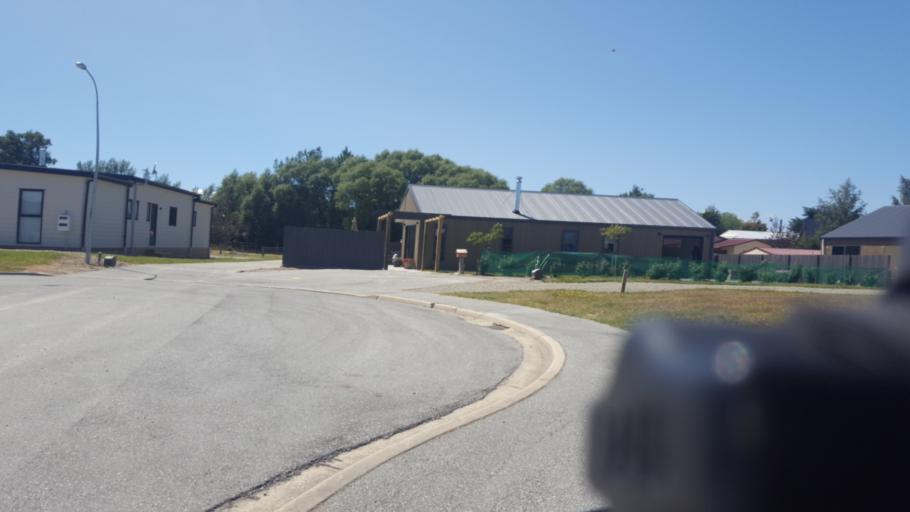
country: NZ
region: Otago
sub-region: Dunedin City
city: Dunedin
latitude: -45.1248
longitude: 170.1088
